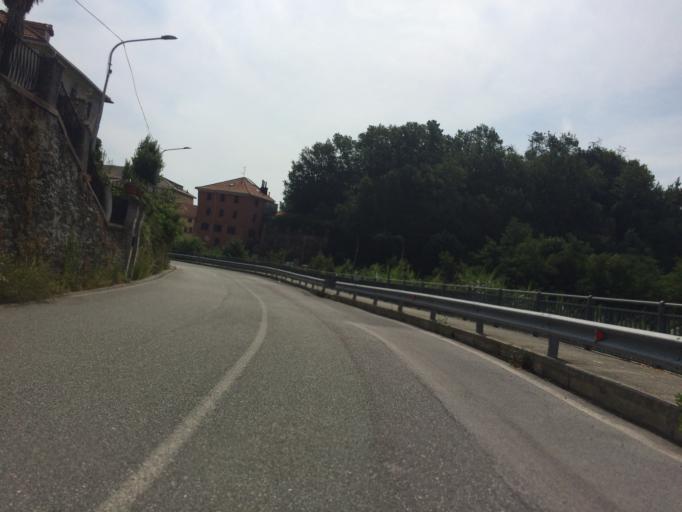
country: IT
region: Liguria
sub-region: Provincia di Savona
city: San Giovanni
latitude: 44.3908
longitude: 8.5136
